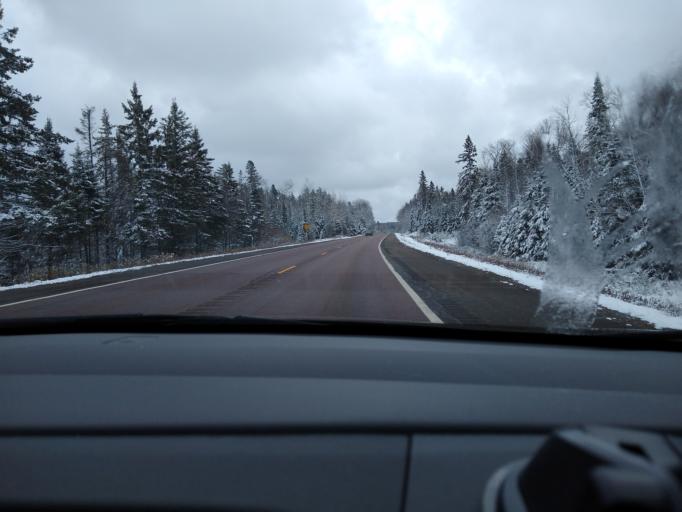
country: US
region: Wisconsin
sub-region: Vilas County
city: Eagle River
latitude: 46.2435
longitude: -89.0957
